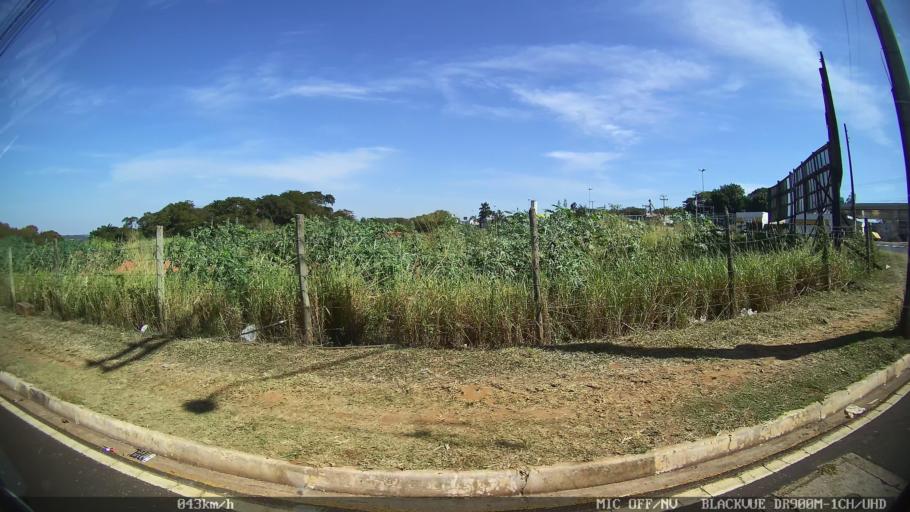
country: BR
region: Sao Paulo
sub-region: Franca
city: Franca
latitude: -20.5436
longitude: -47.4216
